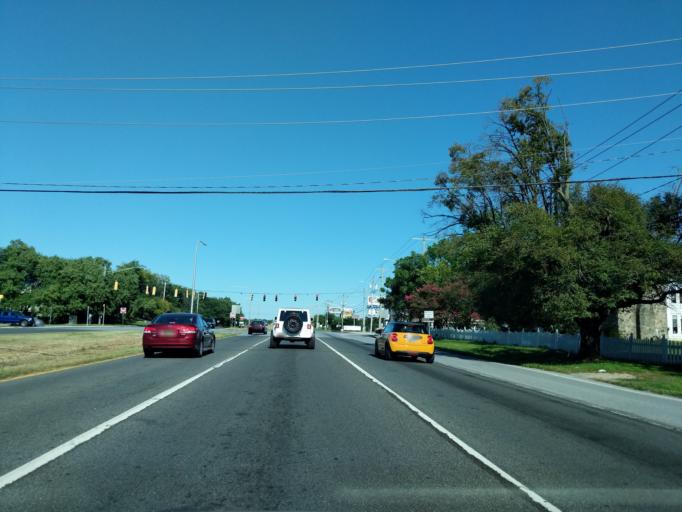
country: US
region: Delaware
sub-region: New Castle County
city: Bear
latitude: 39.6221
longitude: -75.6850
